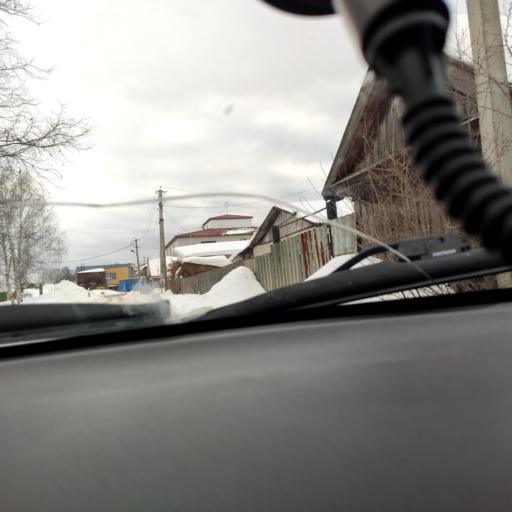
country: RU
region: Tatarstan
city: Osinovo
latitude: 55.8991
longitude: 48.9657
